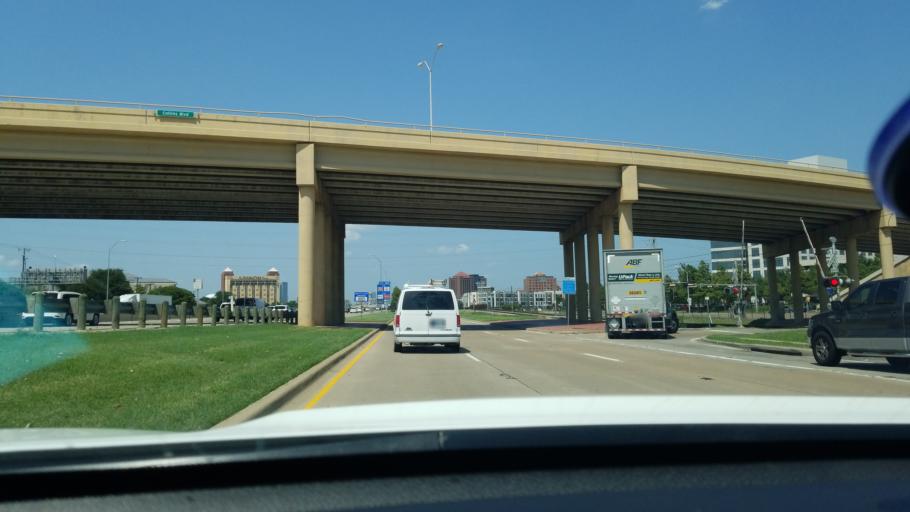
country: US
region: Texas
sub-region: Dallas County
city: Richardson
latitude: 32.9671
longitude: -96.7209
